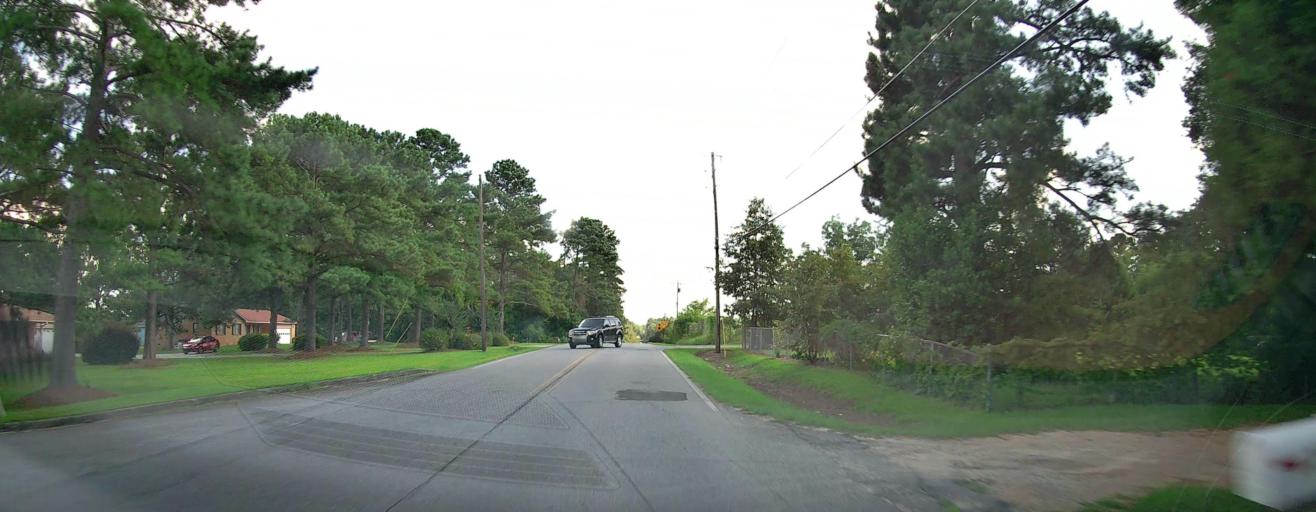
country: US
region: Georgia
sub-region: Houston County
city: Centerville
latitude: 32.6149
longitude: -83.6610
